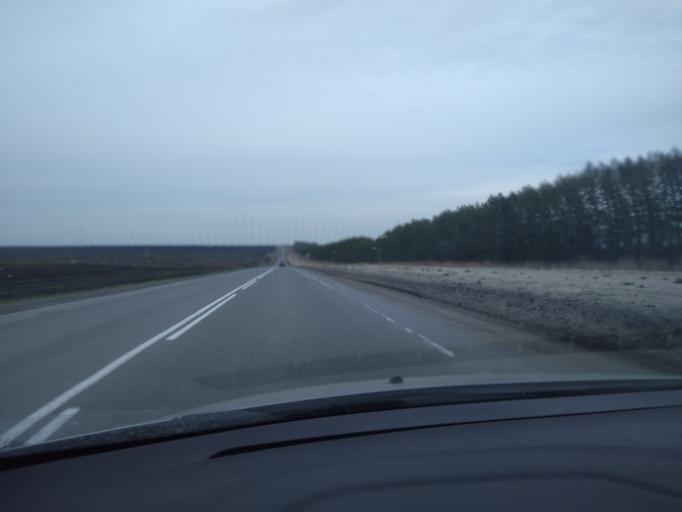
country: RU
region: Sverdlovsk
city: Kamyshlov
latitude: 56.8540
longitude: 62.8759
